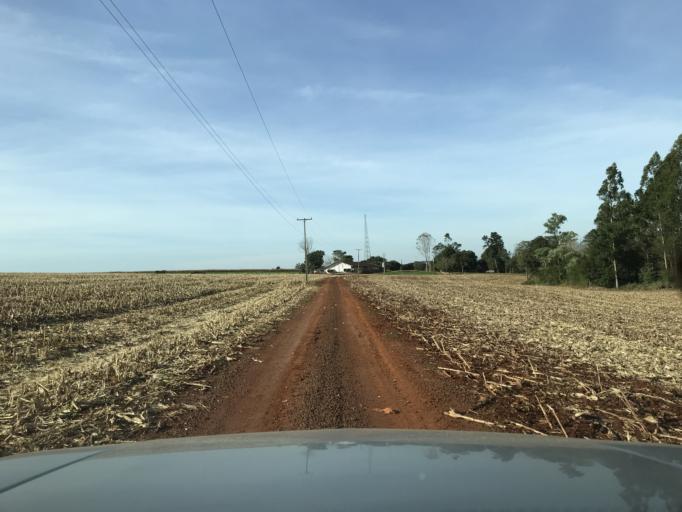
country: BR
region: Parana
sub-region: Palotina
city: Palotina
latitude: -24.2490
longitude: -53.7492
